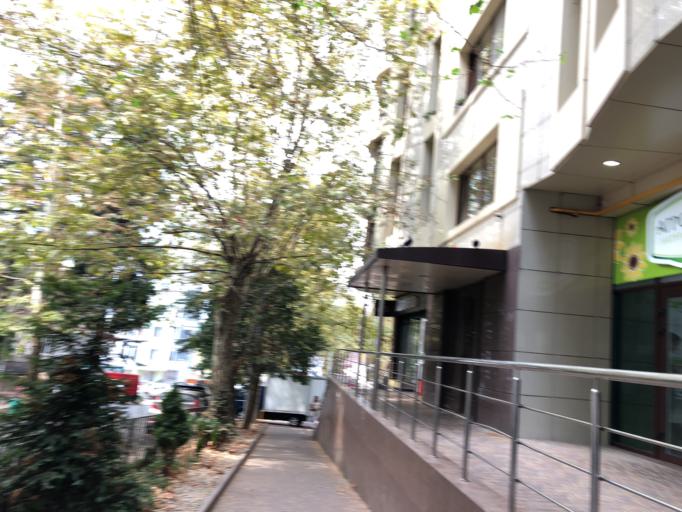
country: RU
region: Krasnodarskiy
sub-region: Sochi City
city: Sochi
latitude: 43.5936
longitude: 39.7369
